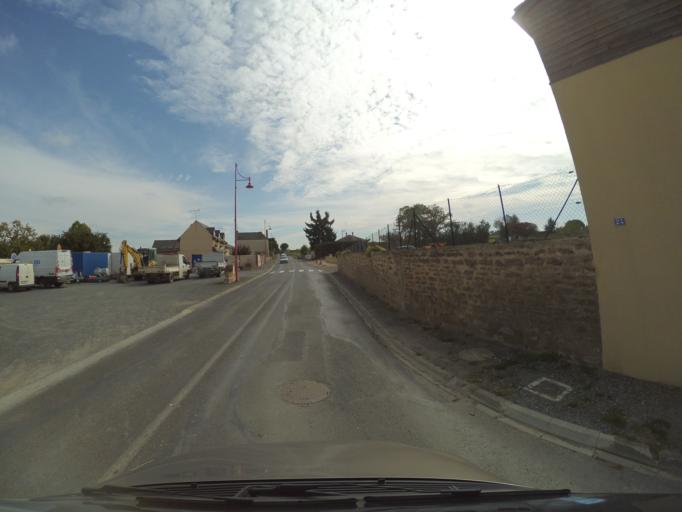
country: FR
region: Pays de la Loire
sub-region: Departement de Maine-et-Loire
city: Saint-Jean
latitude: 47.1974
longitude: -0.3665
